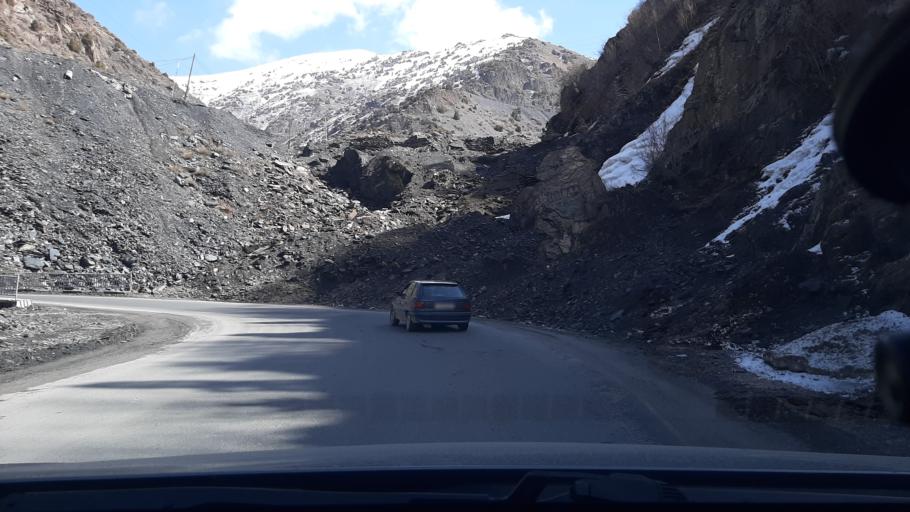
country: TJ
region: Viloyati Sughd
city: Ayni
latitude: 39.5180
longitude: 68.5520
